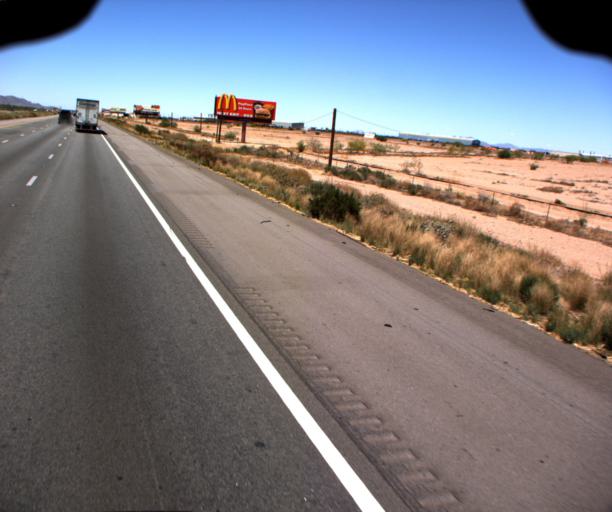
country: US
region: Arizona
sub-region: Pinal County
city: Eloy
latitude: 32.7504
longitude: -111.5760
